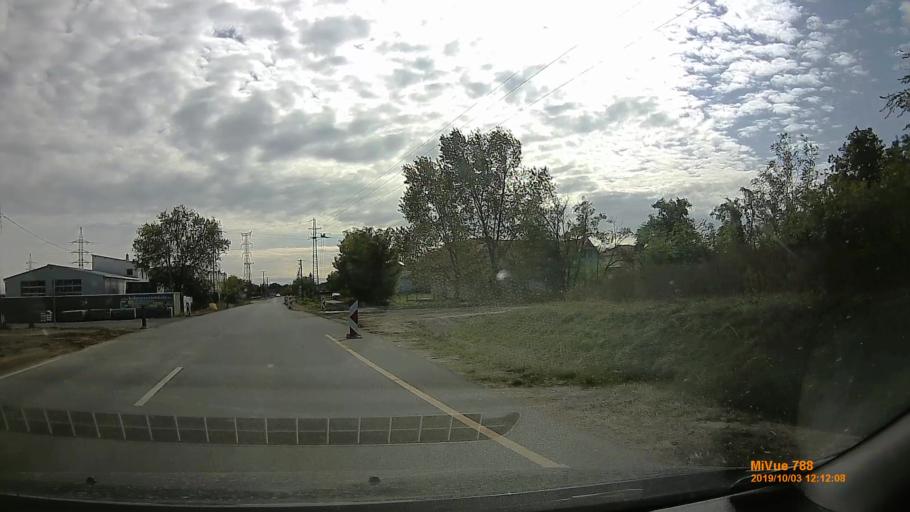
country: HU
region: Pest
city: Szod
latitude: 47.7305
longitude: 19.1649
